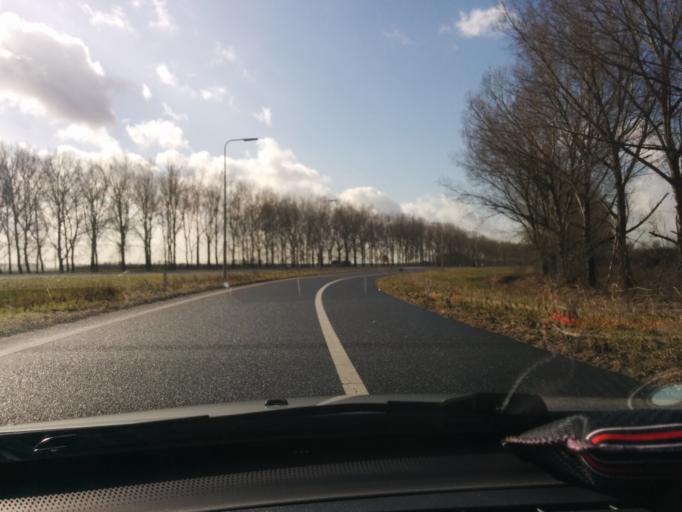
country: NL
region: Flevoland
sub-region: Gemeente Almere
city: Almere Stad
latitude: 52.3975
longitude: 5.3389
